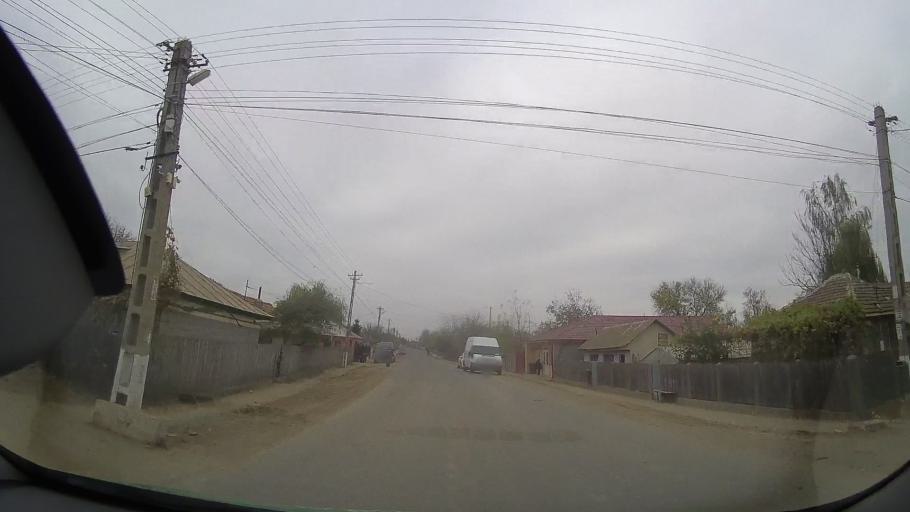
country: RO
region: Buzau
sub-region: Comuna Luciu
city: Luciu
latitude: 44.9721
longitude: 27.0773
